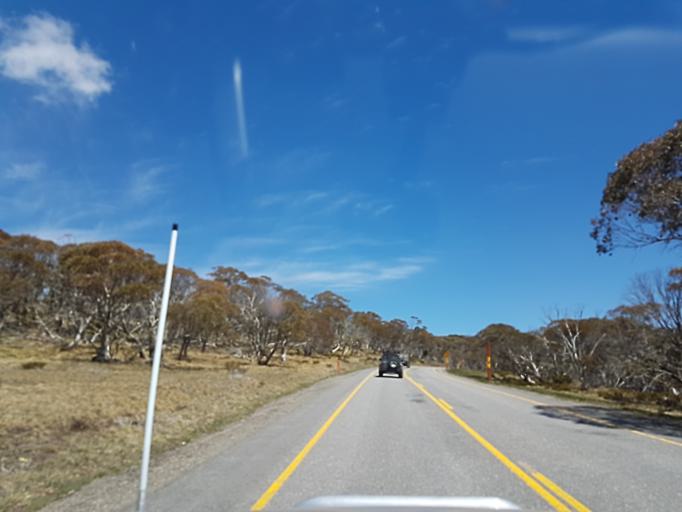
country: AU
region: Victoria
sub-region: Alpine
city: Mount Beauty
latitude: -37.0241
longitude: 147.2167
